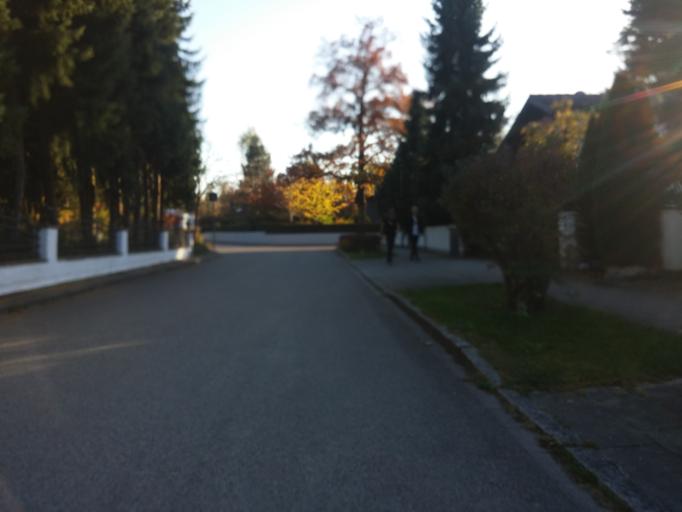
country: DE
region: Bavaria
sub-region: Upper Bavaria
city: Vaterstetten
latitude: 48.0933
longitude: 11.7906
